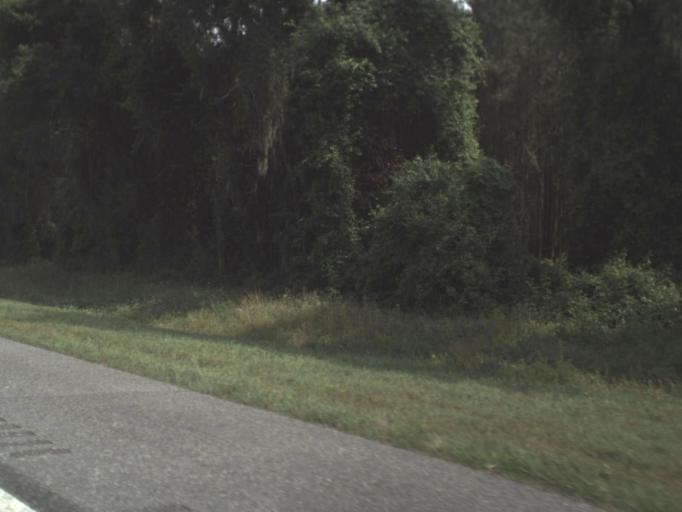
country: US
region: Florida
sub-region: Suwannee County
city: Live Oak
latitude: 30.2963
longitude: -82.8961
